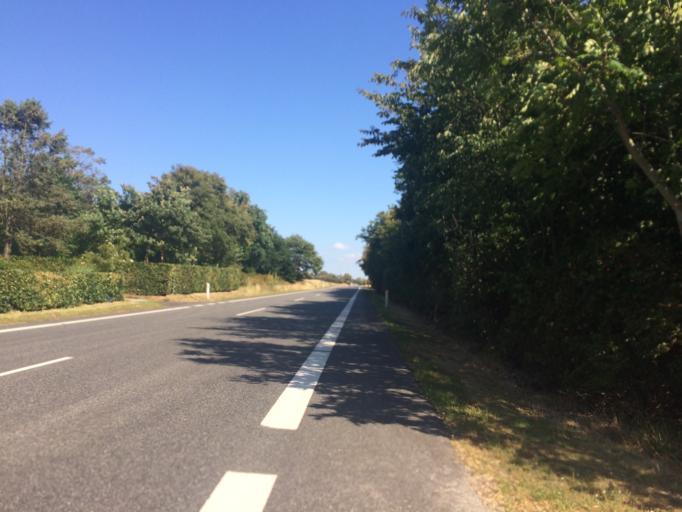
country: DK
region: Central Jutland
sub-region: Holstebro Kommune
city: Vinderup
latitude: 56.5808
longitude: 8.8362
